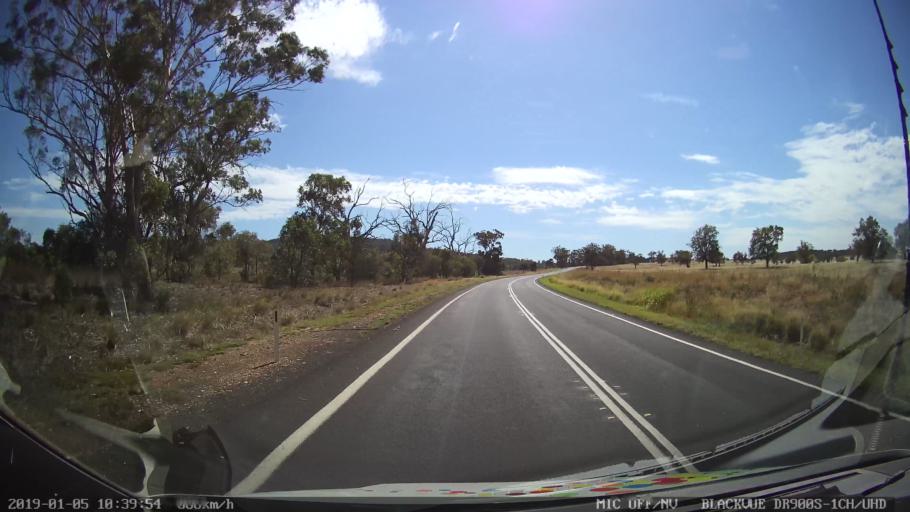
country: AU
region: New South Wales
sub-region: Gilgandra
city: Gilgandra
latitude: -31.4659
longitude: 148.9365
